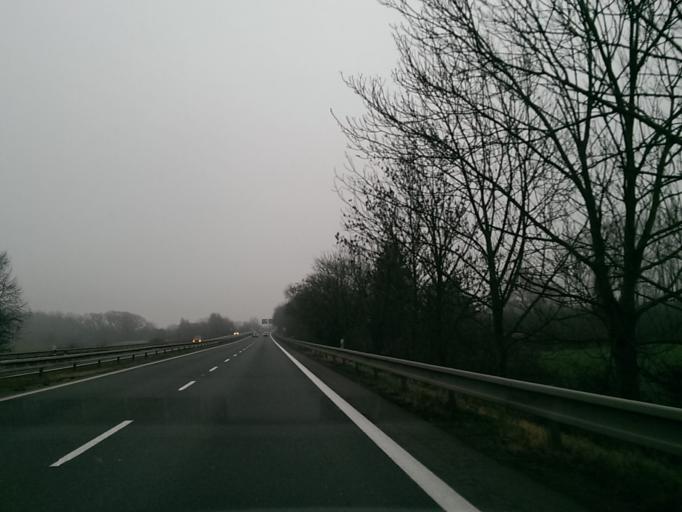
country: CZ
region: Olomoucky
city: Horka nad Moravou
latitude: 49.6081
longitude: 17.2055
